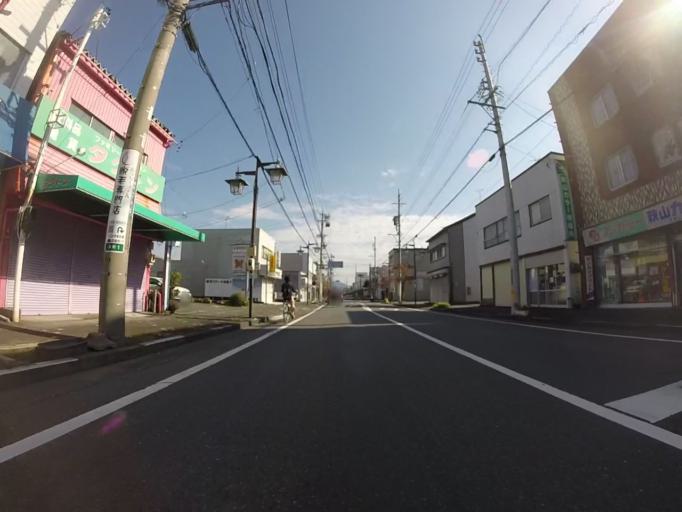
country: JP
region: Shizuoka
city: Fujieda
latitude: 34.8727
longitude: 138.2598
